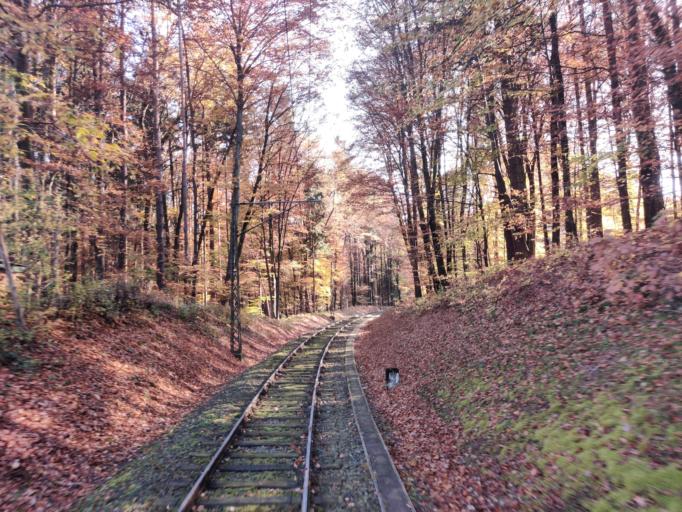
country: AT
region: Styria
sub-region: Politischer Bezirk Suedoststeiermark
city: Trautmannsdorf in Oststeiermark
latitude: 46.8768
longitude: 15.8931
